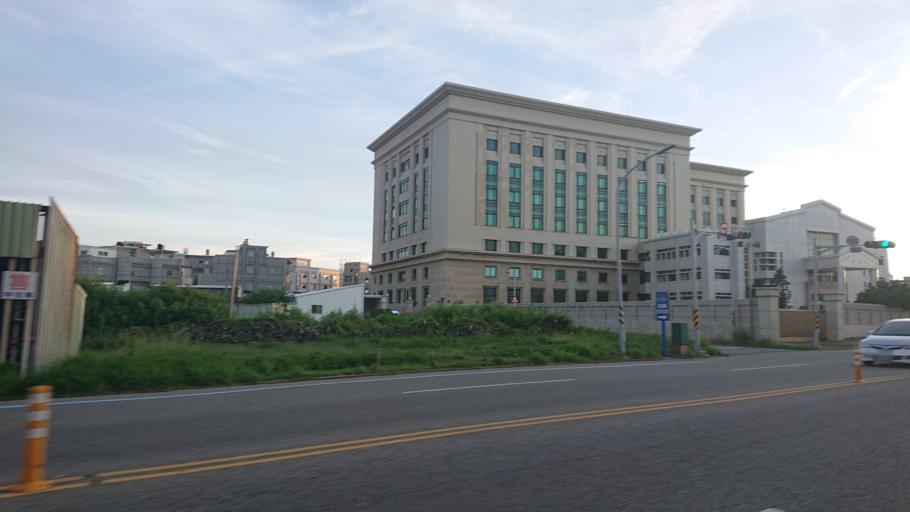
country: TW
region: Taiwan
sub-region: Penghu
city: Ma-kung
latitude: 23.5695
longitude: 119.5850
